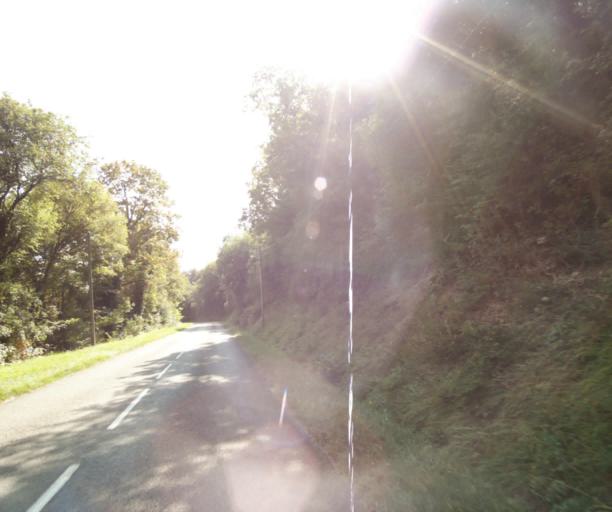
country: FR
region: Bourgogne
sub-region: Departement de Saone-et-Loire
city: Tournus
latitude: 46.5576
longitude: 4.8766
